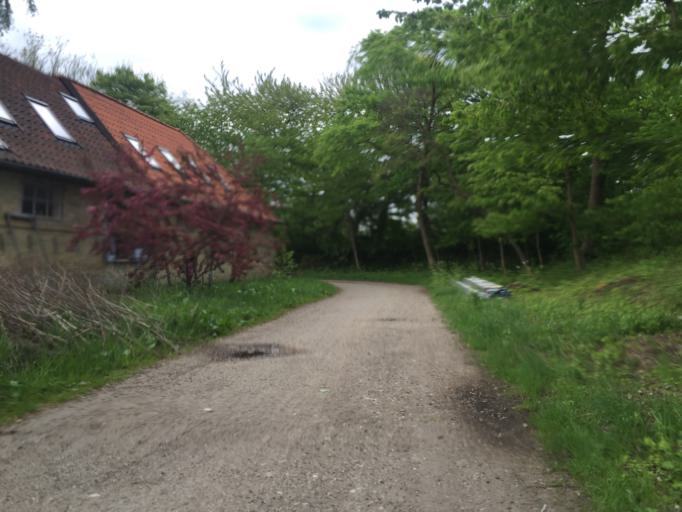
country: DK
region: Capital Region
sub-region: Kobenhavn
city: Christianshavn
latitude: 55.6767
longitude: 12.6115
